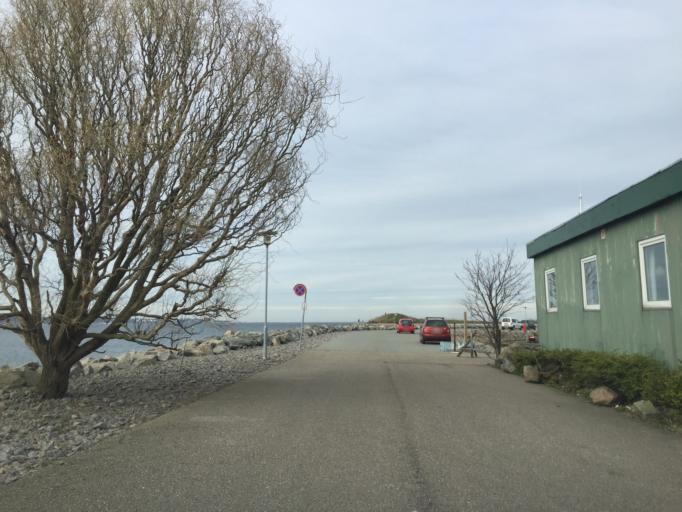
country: DK
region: Capital Region
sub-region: Gentofte Kommune
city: Charlottenlund
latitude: 55.7237
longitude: 12.6017
